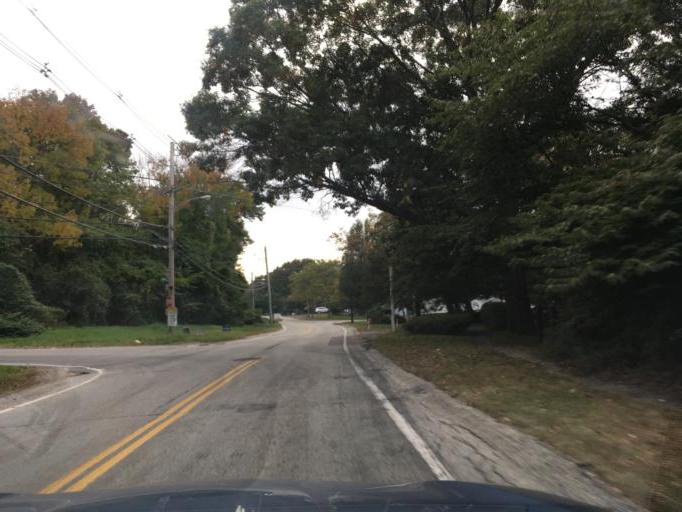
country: US
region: Rhode Island
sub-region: Kent County
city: East Greenwich
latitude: 41.6854
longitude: -71.4629
